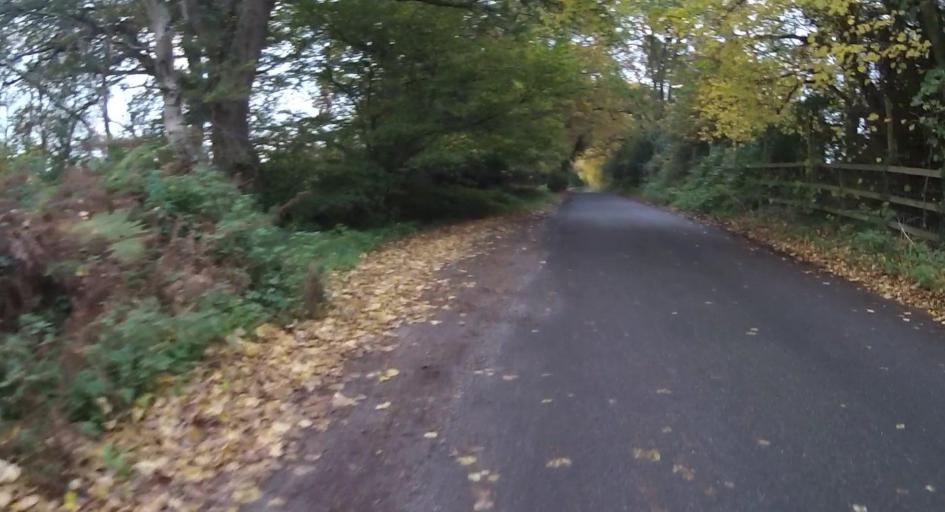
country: GB
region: England
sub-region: Surrey
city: Churt
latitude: 51.1461
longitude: -0.7980
